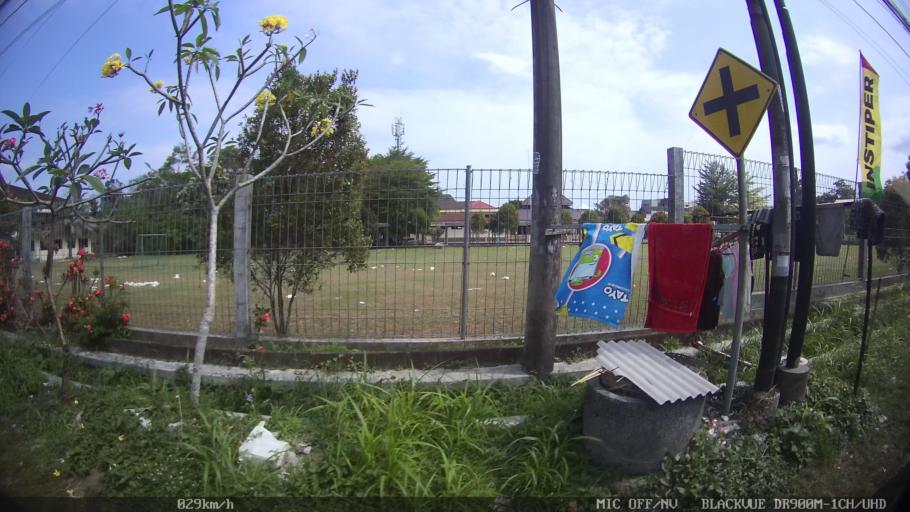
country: ID
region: Daerah Istimewa Yogyakarta
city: Depok
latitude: -7.7598
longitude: 110.4253
